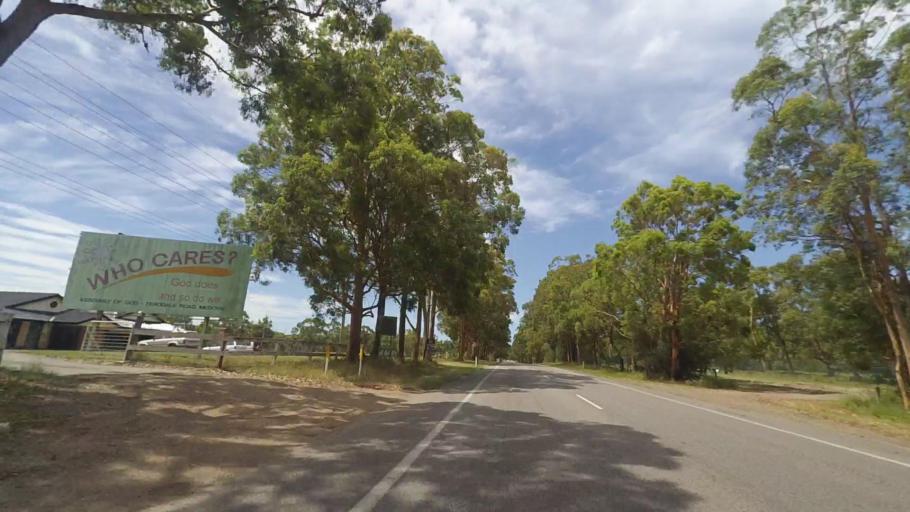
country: AU
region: New South Wales
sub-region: Port Stephens Shire
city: Medowie
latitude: -32.7706
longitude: 151.8611
